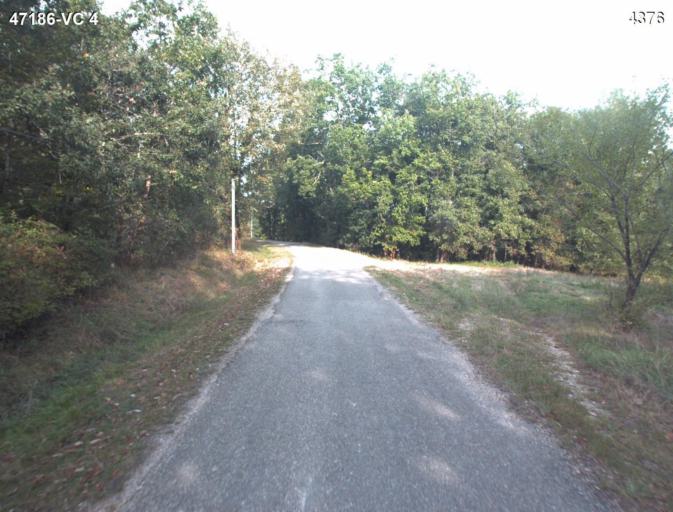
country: FR
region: Aquitaine
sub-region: Departement du Lot-et-Garonne
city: Sainte-Colombe-en-Bruilhois
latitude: 44.1944
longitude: 0.4511
